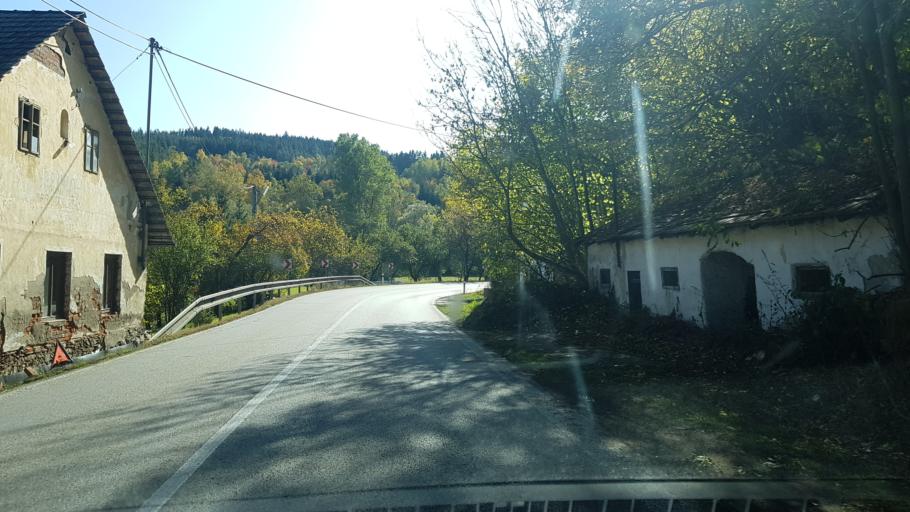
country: CZ
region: Jihocesky
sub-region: Okres Prachatice
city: Vimperk
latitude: 49.0883
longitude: 13.7940
